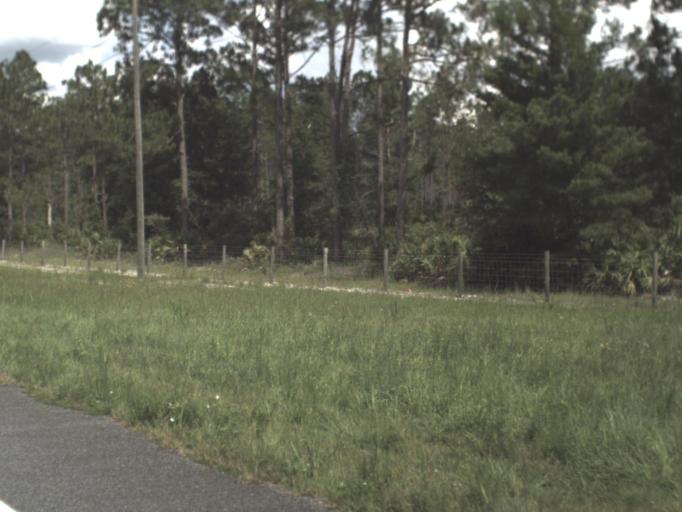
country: US
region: Florida
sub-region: Bradford County
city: Starke
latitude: 29.9581
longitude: -82.0314
